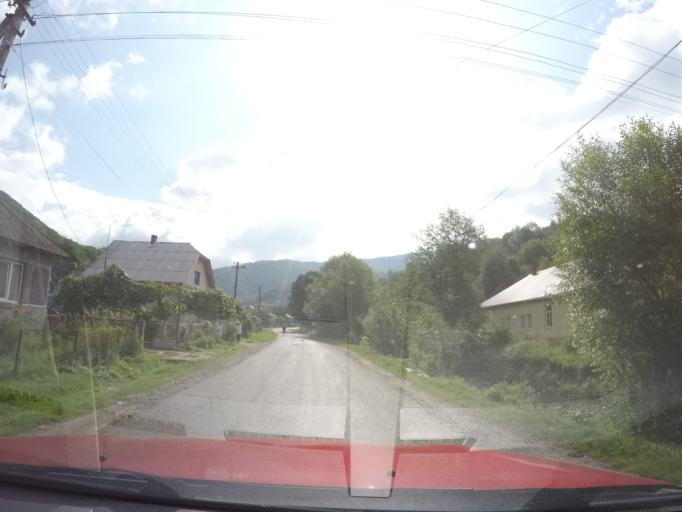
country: UA
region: Zakarpattia
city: Velykyi Bereznyi
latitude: 48.9425
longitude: 22.6241
